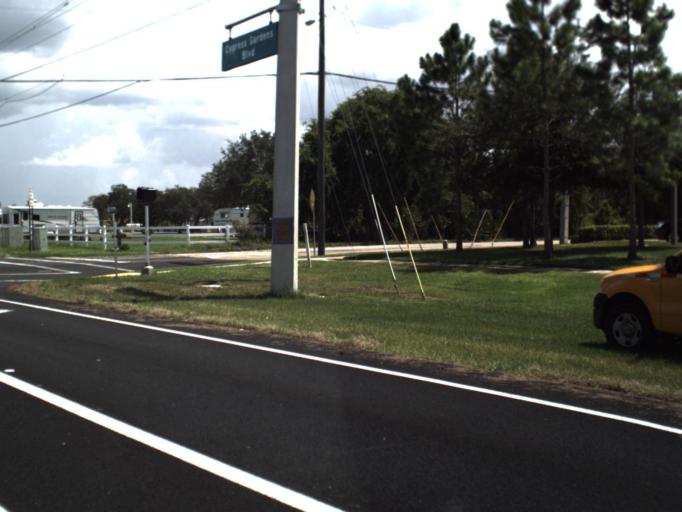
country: US
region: Florida
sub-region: Polk County
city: Cypress Gardens
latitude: 27.9784
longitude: -81.6530
